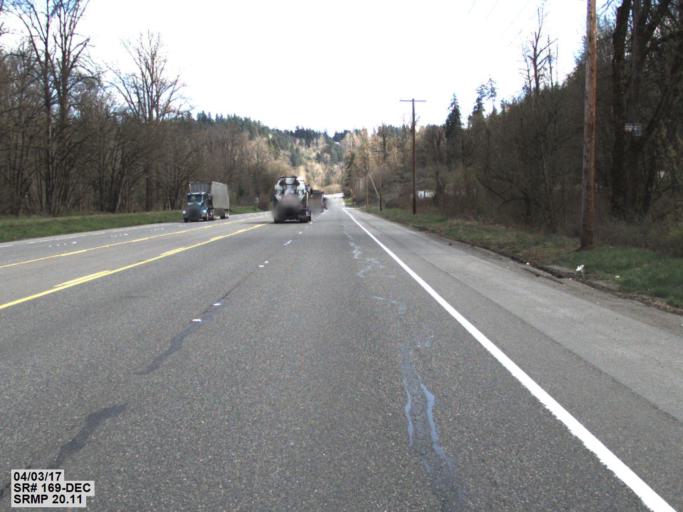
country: US
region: Washington
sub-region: King County
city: Maple Heights-Lake Desire
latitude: 47.4622
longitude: -122.0959
